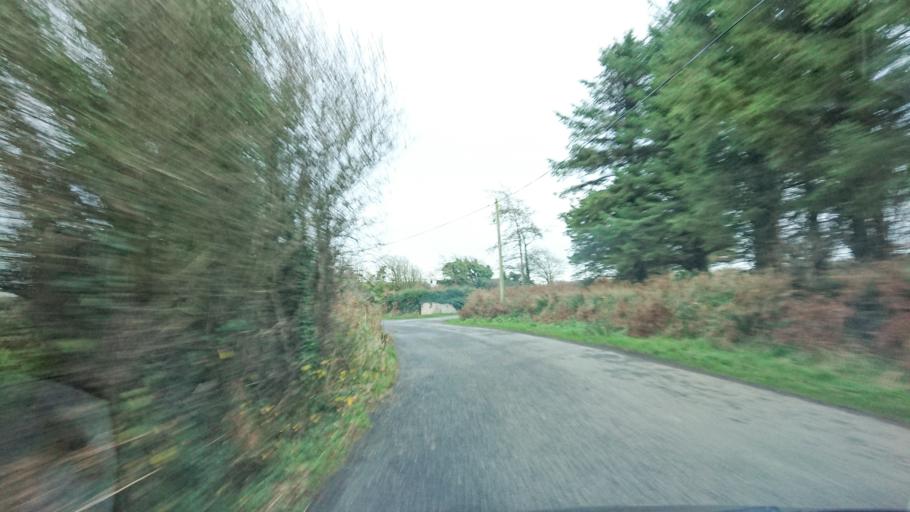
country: IE
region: Munster
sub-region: Waterford
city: Dunmore East
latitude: 52.2381
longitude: -6.9885
